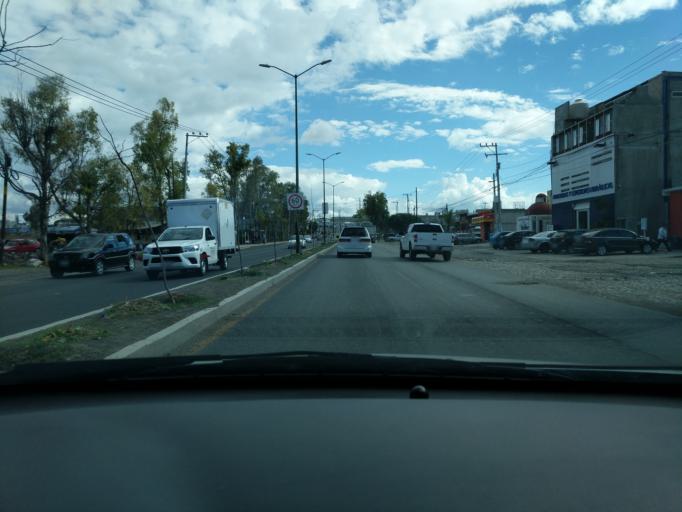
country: MX
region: Queretaro
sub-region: El Marques
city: General Lazaro Cardenas (El Colorado)
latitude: 20.5762
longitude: -100.2572
